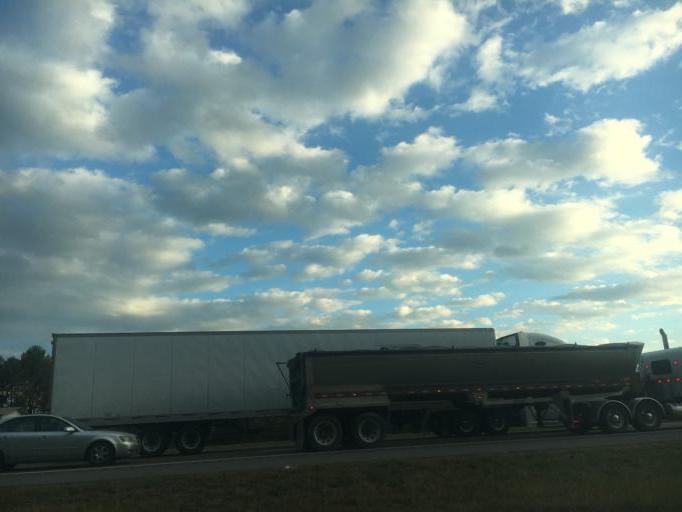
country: US
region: Tennessee
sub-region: Sullivan County
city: Colonial Heights
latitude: 36.4771
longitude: -82.4880
